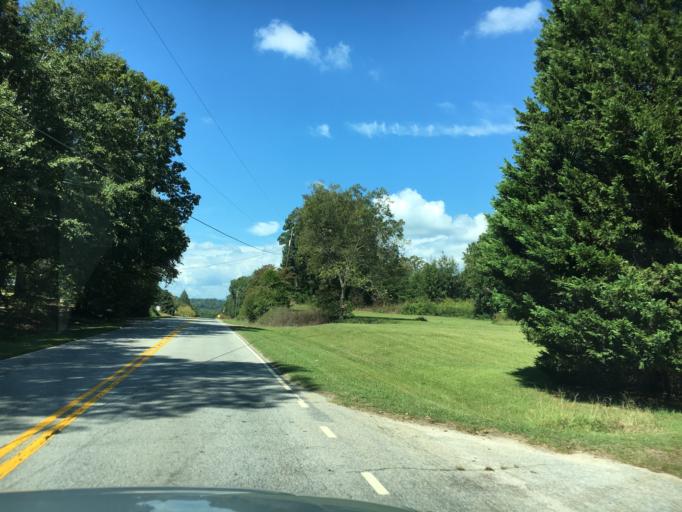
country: US
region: South Carolina
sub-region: Greenville County
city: Tigerville
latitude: 35.0247
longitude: -82.3995
